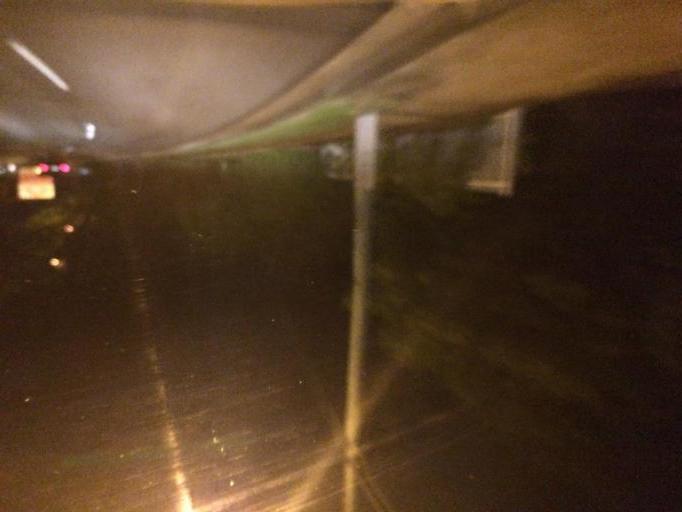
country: AU
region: Queensland
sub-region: Brisbane
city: Kenmore Hills
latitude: -27.5094
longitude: 152.9459
